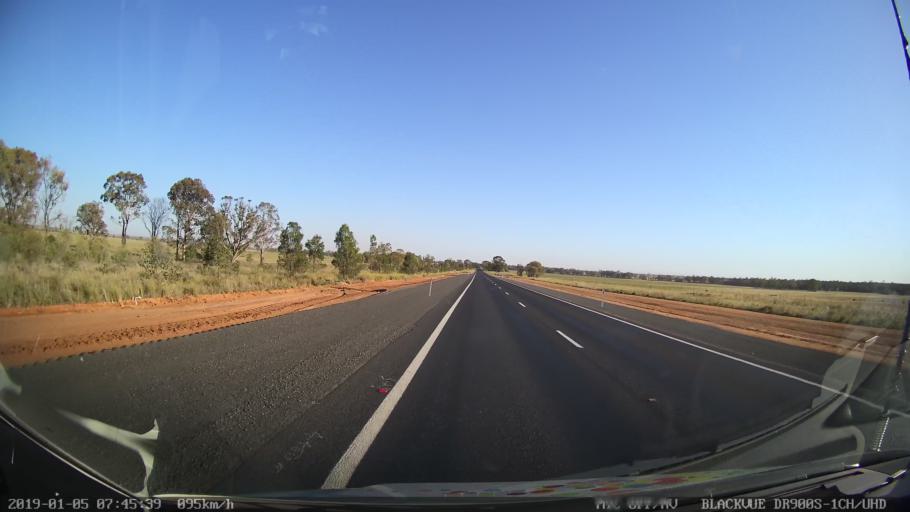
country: AU
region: New South Wales
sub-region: Gilgandra
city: Gilgandra
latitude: -31.8554
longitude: 148.6435
